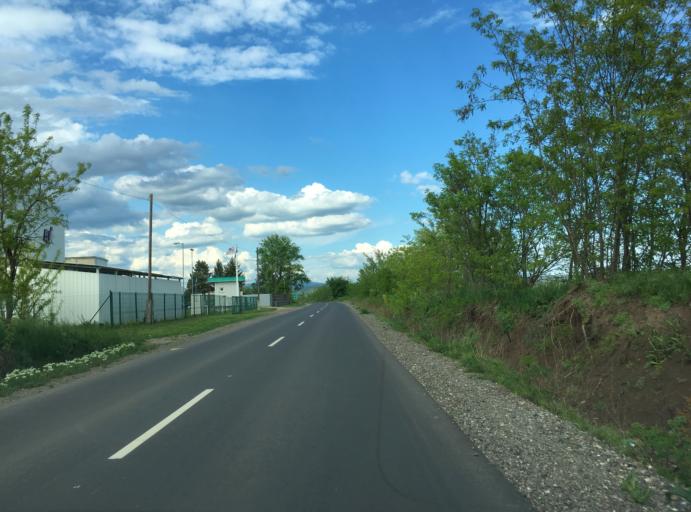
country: HU
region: Heves
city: Lorinci
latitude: 47.7261
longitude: 19.6583
